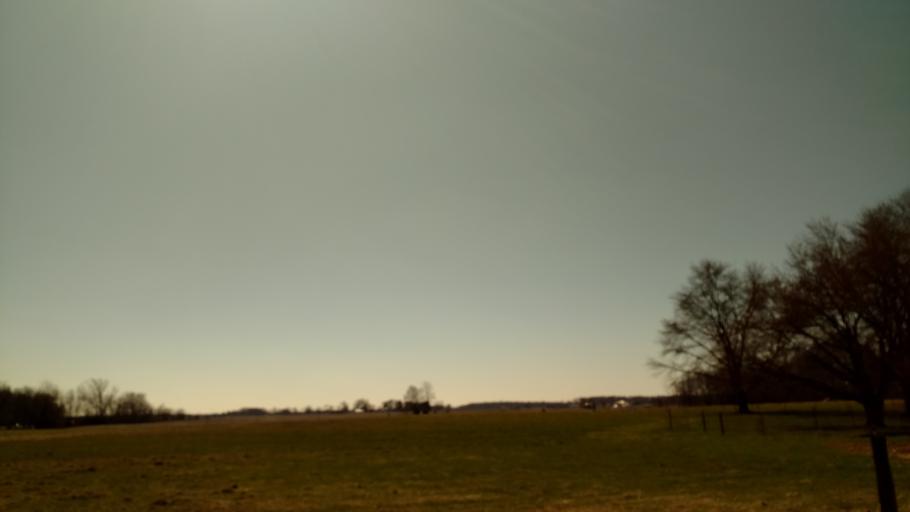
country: US
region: Ohio
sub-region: Marion County
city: Marion
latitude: 40.4936
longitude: -83.0759
